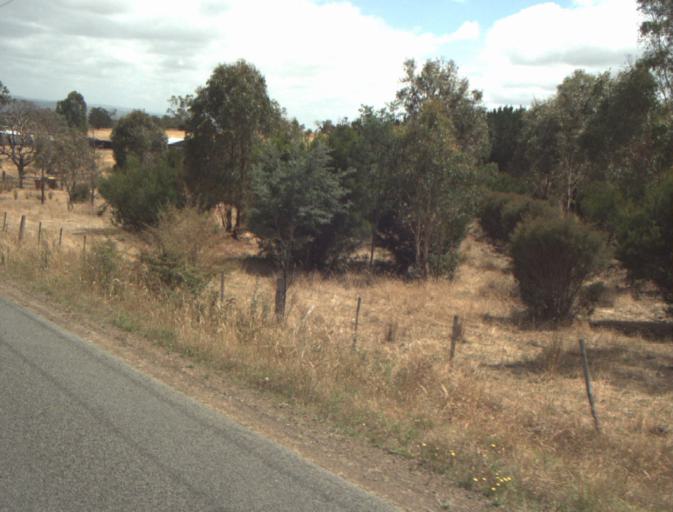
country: AU
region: Tasmania
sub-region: Northern Midlands
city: Evandale
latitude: -41.5086
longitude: 147.2818
